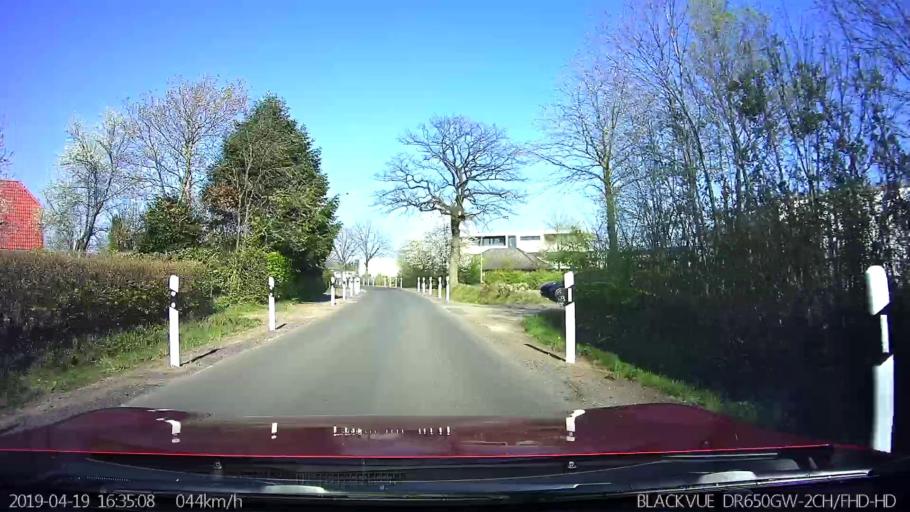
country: DE
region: Schleswig-Holstein
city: Tangstedt
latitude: 53.6673
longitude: 9.8362
